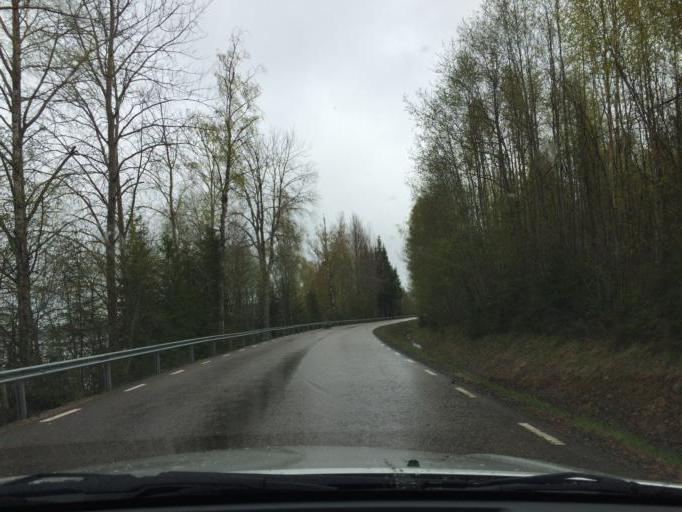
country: SE
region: Dalarna
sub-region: Ludvika Kommun
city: Grangesberg
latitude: 60.0530
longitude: 14.8941
